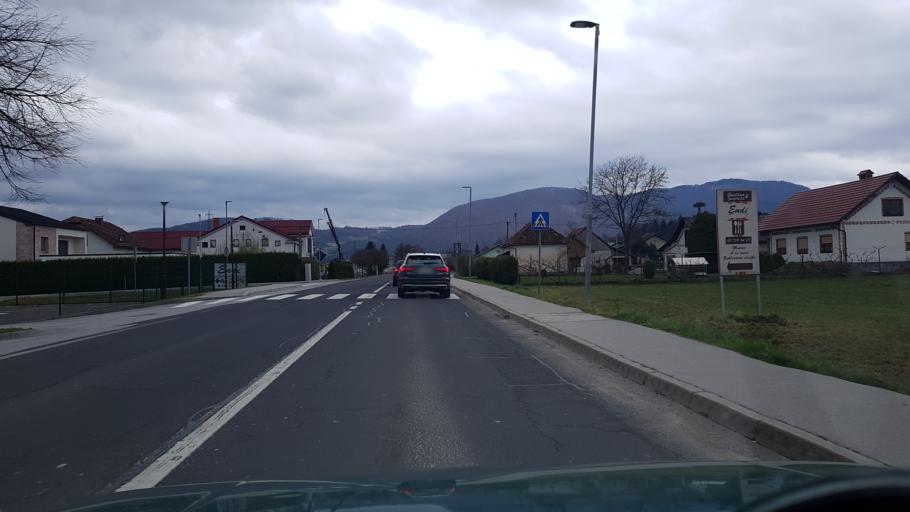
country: SI
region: Slovenska Konjice
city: Slovenske Konjice
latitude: 46.3450
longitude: 15.4741
